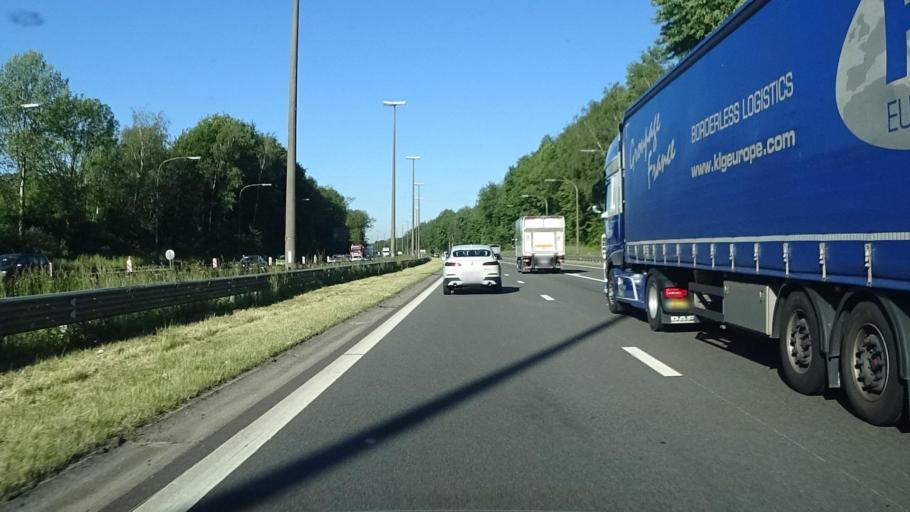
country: BE
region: Wallonia
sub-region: Province du Hainaut
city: Seneffe
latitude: 50.5397
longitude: 4.2287
